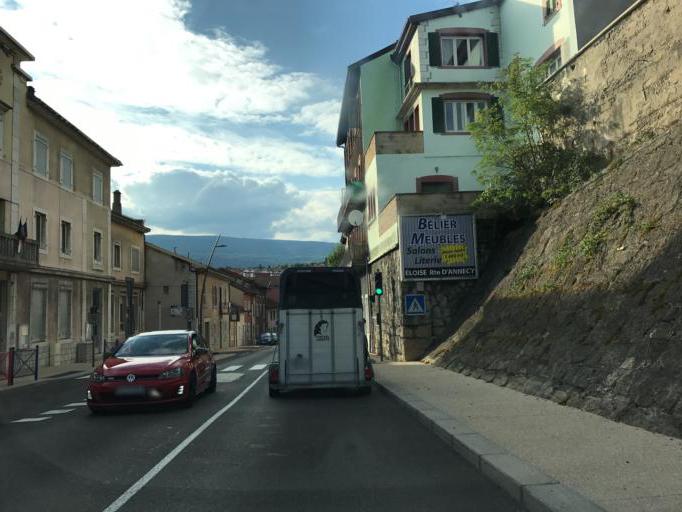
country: FR
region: Rhone-Alpes
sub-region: Departement de l'Ain
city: Bellegarde-sur-Valserine
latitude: 46.1071
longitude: 5.8332
